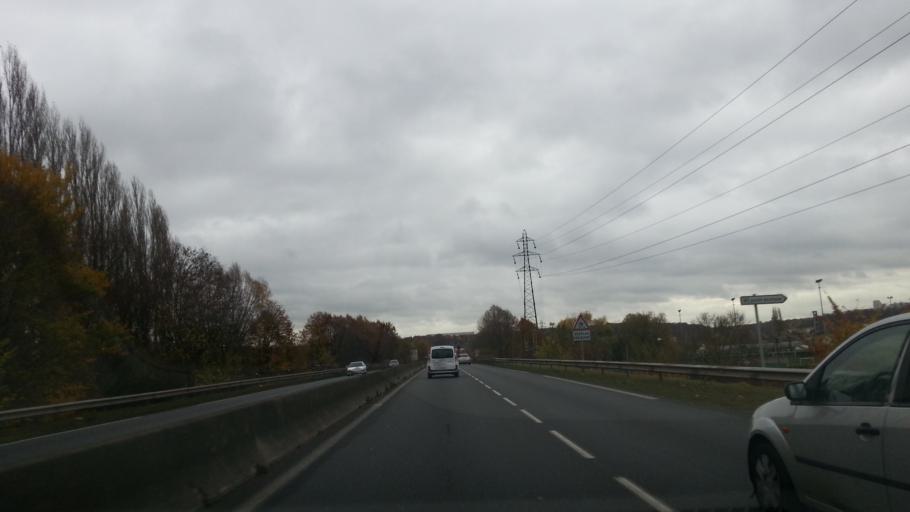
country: FR
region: Picardie
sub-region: Departement de l'Oise
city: Villers-Saint-Paul
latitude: 49.2795
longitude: 2.4817
